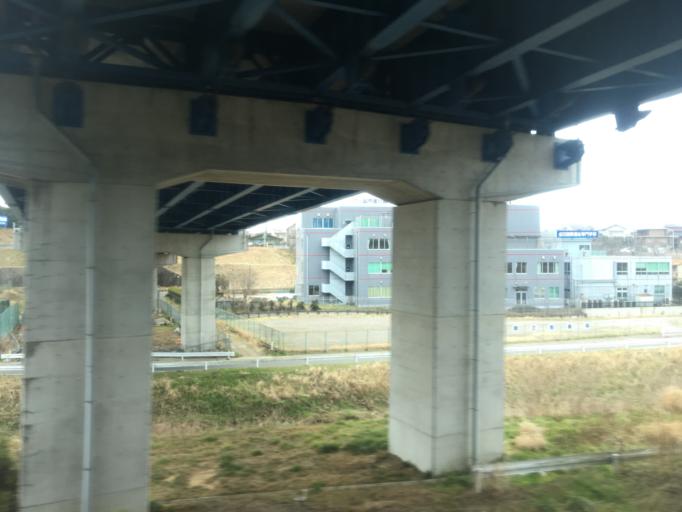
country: JP
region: Chiba
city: Narita
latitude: 35.7853
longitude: 140.3057
